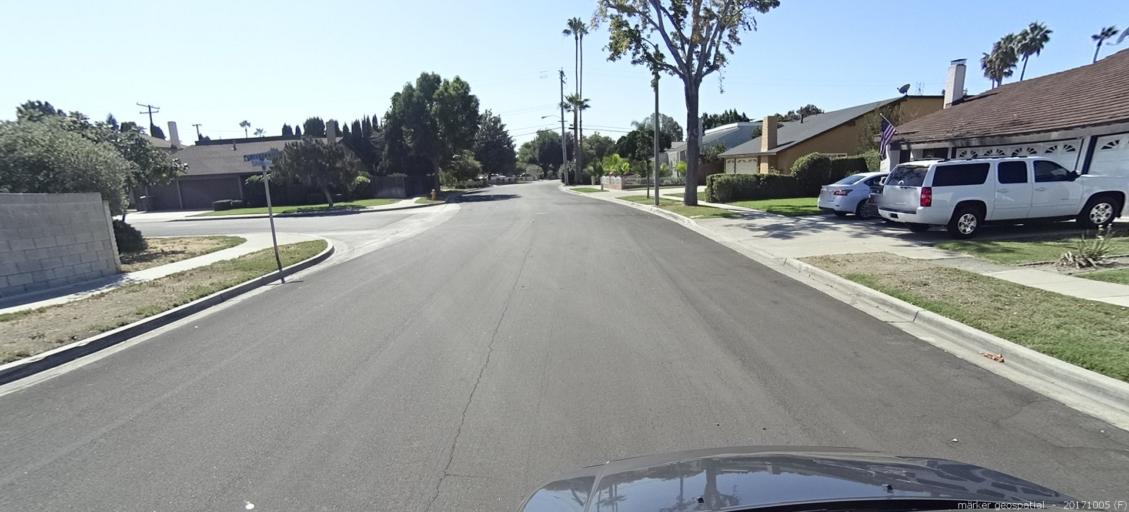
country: US
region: California
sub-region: Orange County
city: Stanton
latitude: 33.8021
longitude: -117.9734
